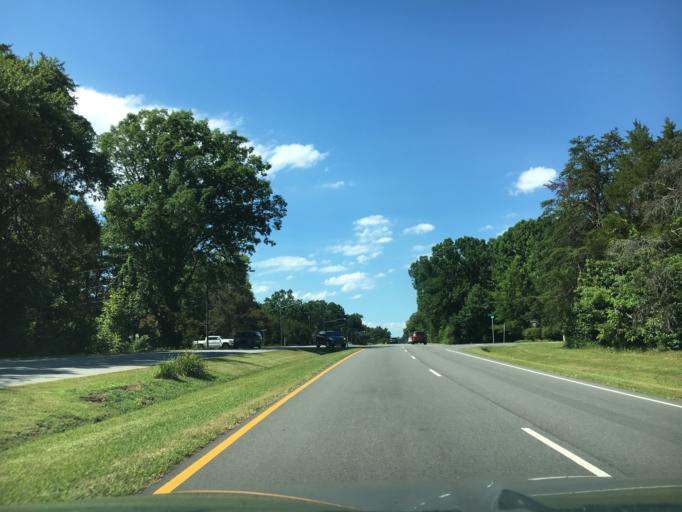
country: US
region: Virginia
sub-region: Halifax County
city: South Boston
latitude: 36.7200
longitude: -78.9177
